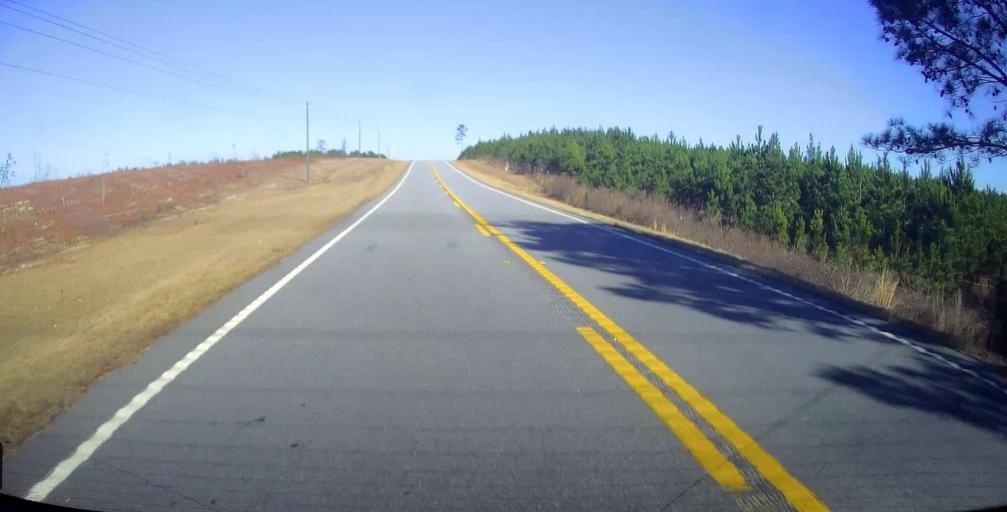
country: US
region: Georgia
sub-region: Taylor County
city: Butler
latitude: 32.5822
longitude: -84.2005
